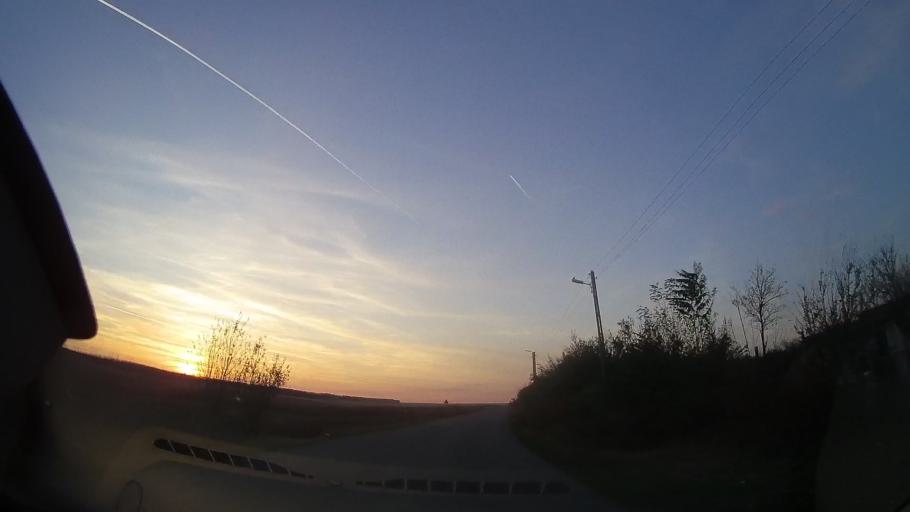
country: RO
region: Constanta
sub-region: Comuna Mereni
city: Mereni
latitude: 44.0155
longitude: 28.3132
